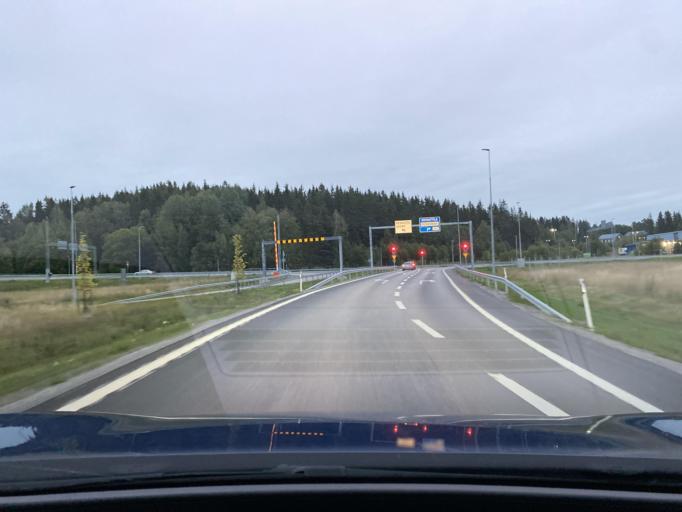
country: FI
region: Paijanne Tavastia
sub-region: Lahti
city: Lahti
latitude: 60.9558
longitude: 25.6490
